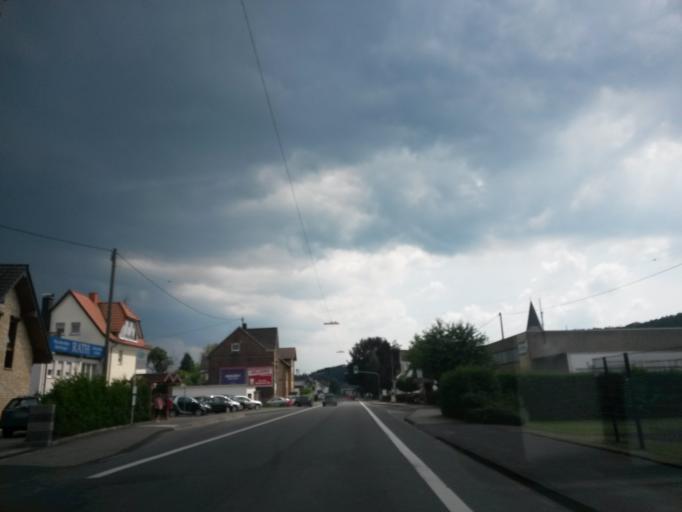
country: DE
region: North Rhine-Westphalia
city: Kreuztal
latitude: 50.9417
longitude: 8.0006
